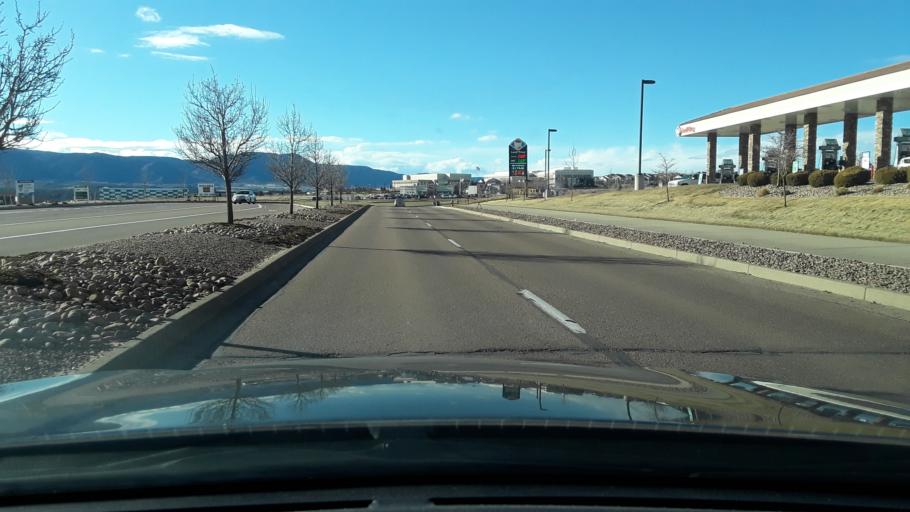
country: US
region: Colorado
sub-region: El Paso County
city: Gleneagle
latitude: 39.0209
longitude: -104.8139
